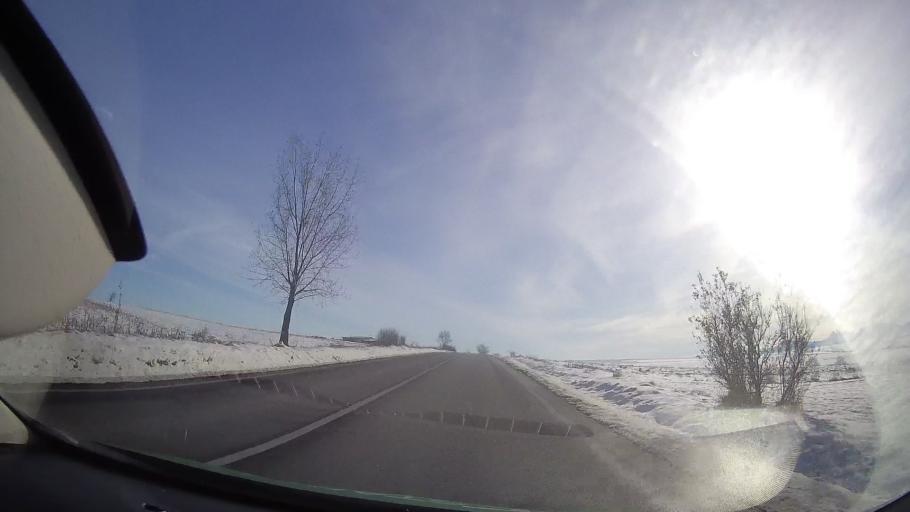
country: RO
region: Neamt
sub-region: Comuna Baltatesti
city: Valea Seaca
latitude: 47.1609
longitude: 26.3189
